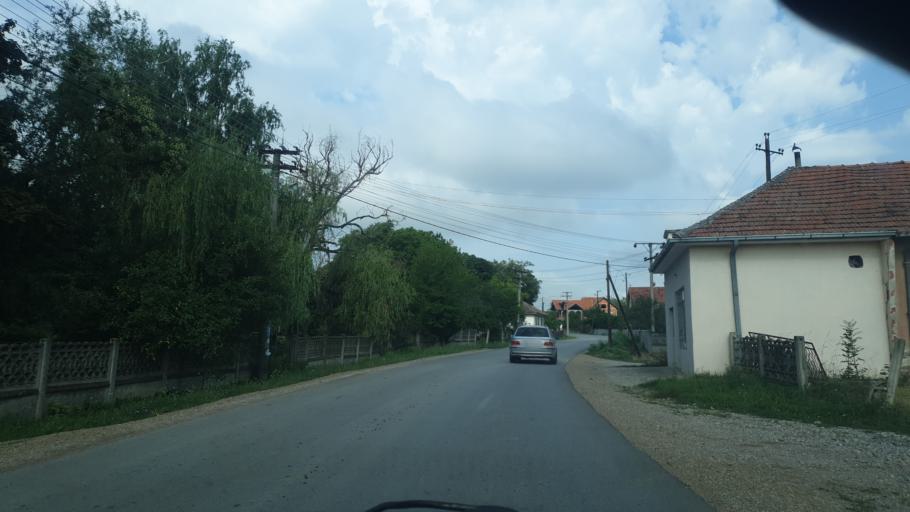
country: RS
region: Central Serbia
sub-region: Sumadijski Okrug
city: Kragujevac
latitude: 44.1076
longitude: 20.8145
